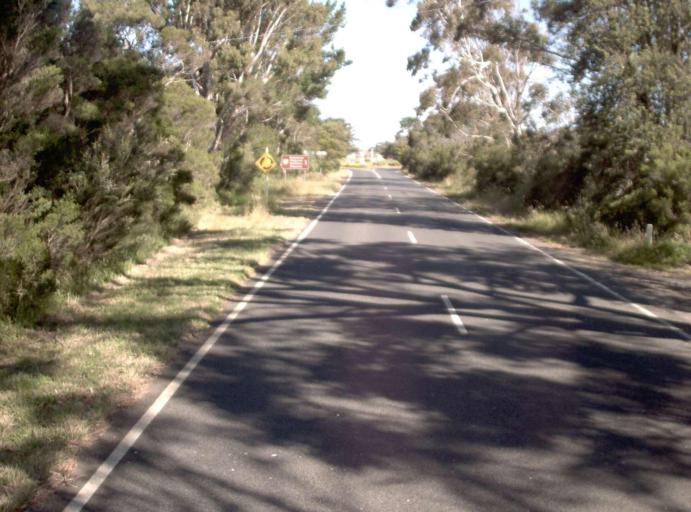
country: AU
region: Victoria
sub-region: Latrobe
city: Traralgon
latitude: -38.6640
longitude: 146.6869
